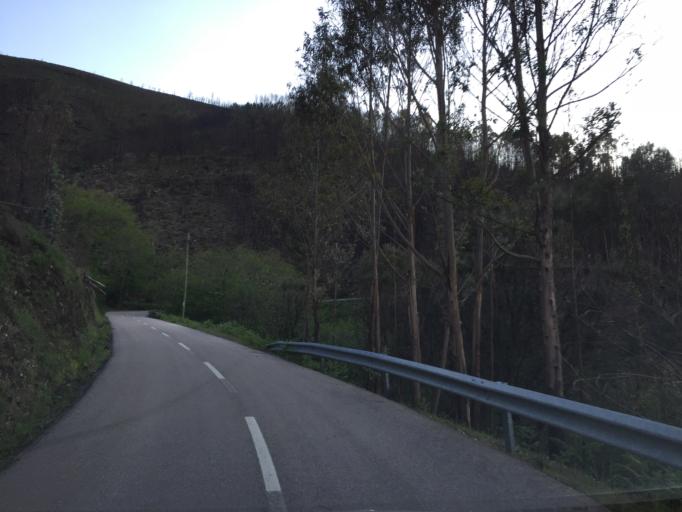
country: PT
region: Coimbra
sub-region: Arganil
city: Arganil
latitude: 40.1294
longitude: -8.0109
